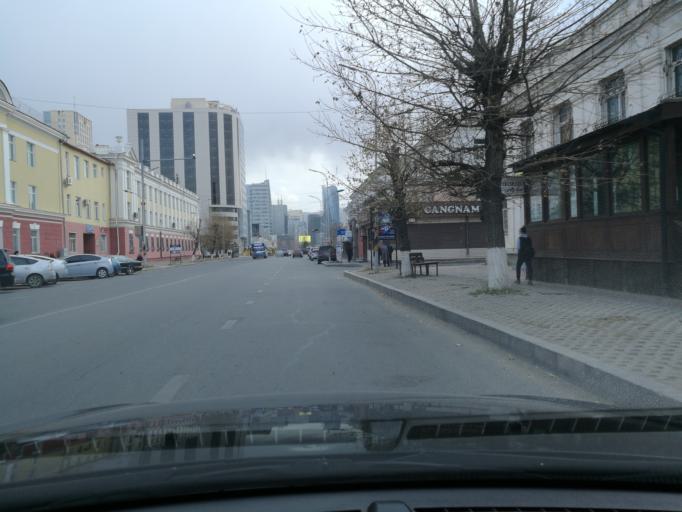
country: MN
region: Ulaanbaatar
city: Ulaanbaatar
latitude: 47.9238
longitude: 106.9181
